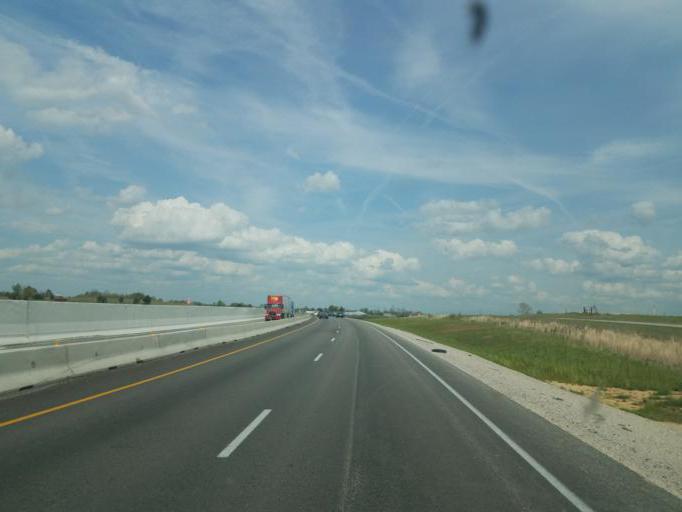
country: US
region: Kentucky
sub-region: Larue County
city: Hodgenville
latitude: 37.4912
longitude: -85.8807
